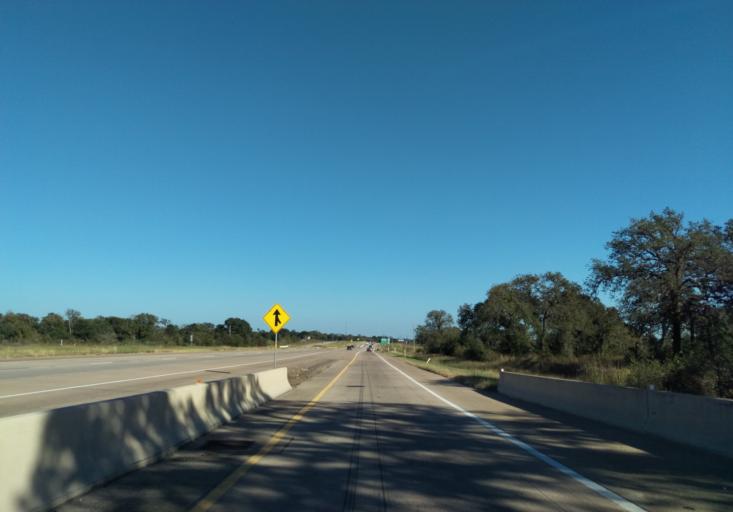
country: US
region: Texas
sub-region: Waller County
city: Hempstead
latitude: 30.1133
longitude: -96.0686
